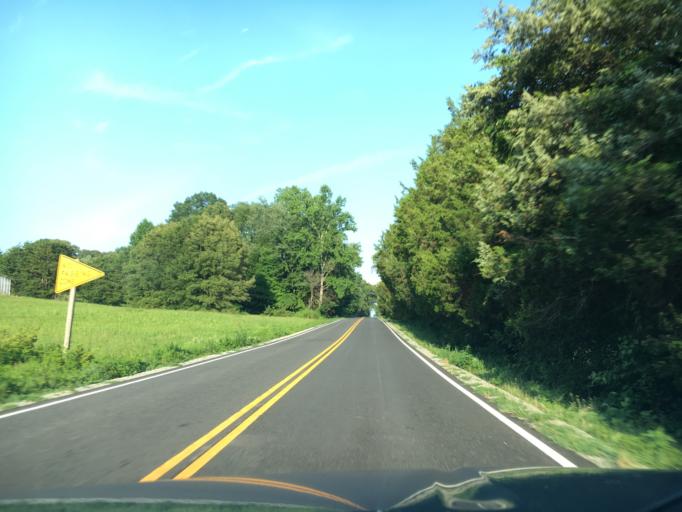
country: US
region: Virginia
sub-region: Pittsylvania County
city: Chatham
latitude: 36.8191
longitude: -79.3658
